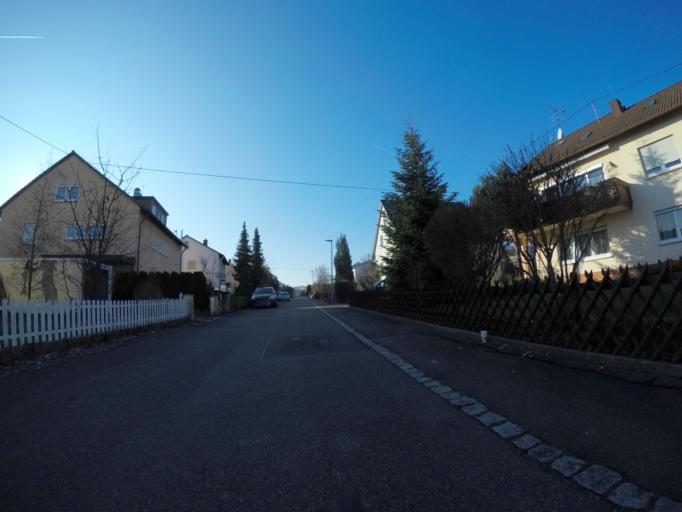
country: DE
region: Baden-Wuerttemberg
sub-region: Tuebingen Region
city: Reutlingen
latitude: 48.5171
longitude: 9.2226
